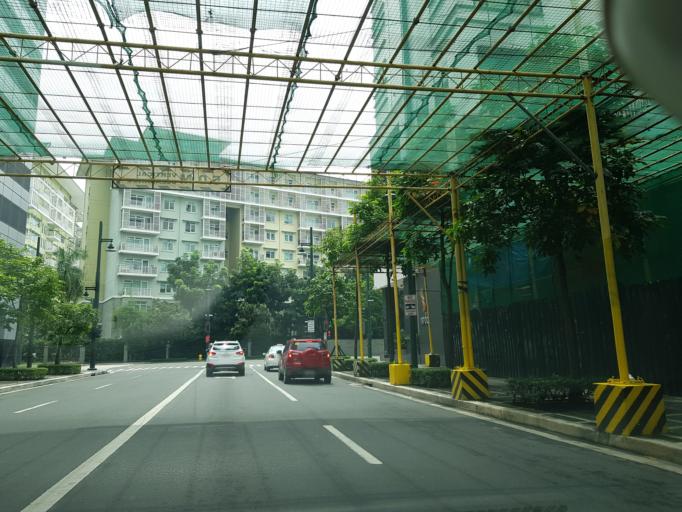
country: PH
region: Metro Manila
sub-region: Makati City
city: Makati City
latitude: 14.5511
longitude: 121.0529
